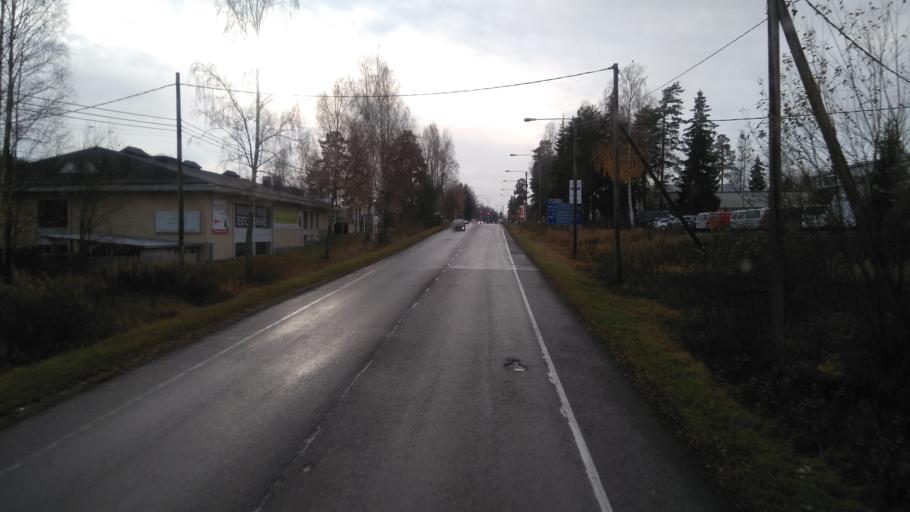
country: FI
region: Uusimaa
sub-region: Porvoo
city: Porvoo
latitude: 60.4050
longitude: 25.6906
